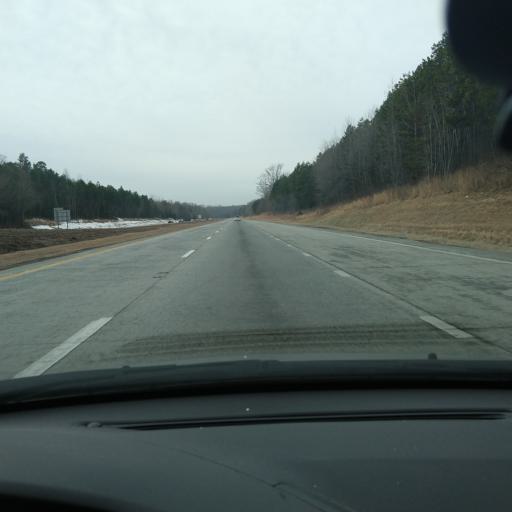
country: US
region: North Carolina
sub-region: Davidson County
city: Welcome
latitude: 35.8731
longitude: -80.2496
